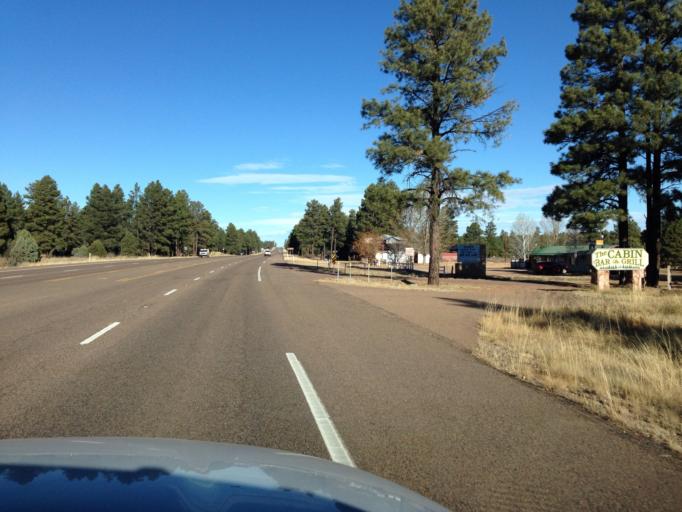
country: US
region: Arizona
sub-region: Navajo County
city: Heber-Overgaard
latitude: 34.3941
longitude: -110.5574
